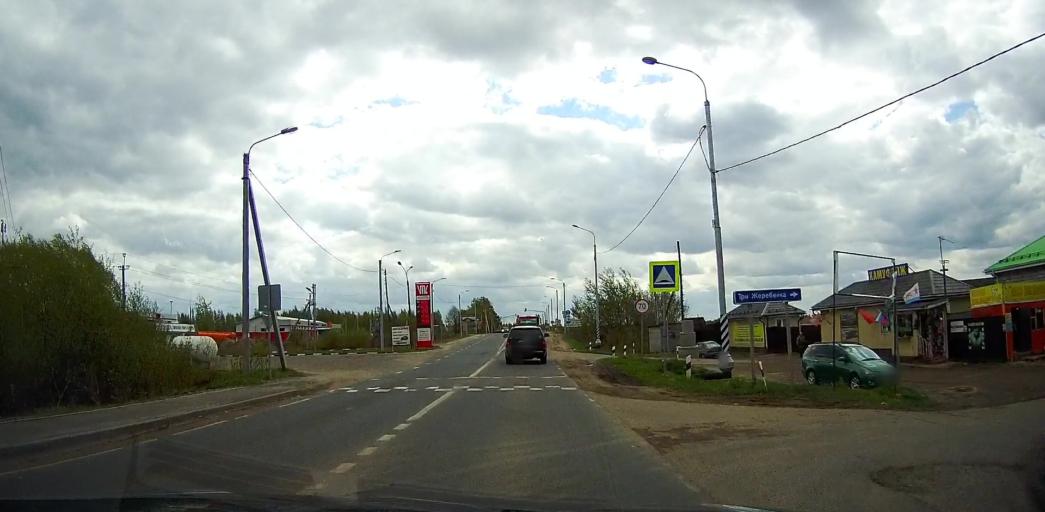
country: RU
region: Moskovskaya
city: Beloozerskiy
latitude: 55.4595
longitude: 38.4238
